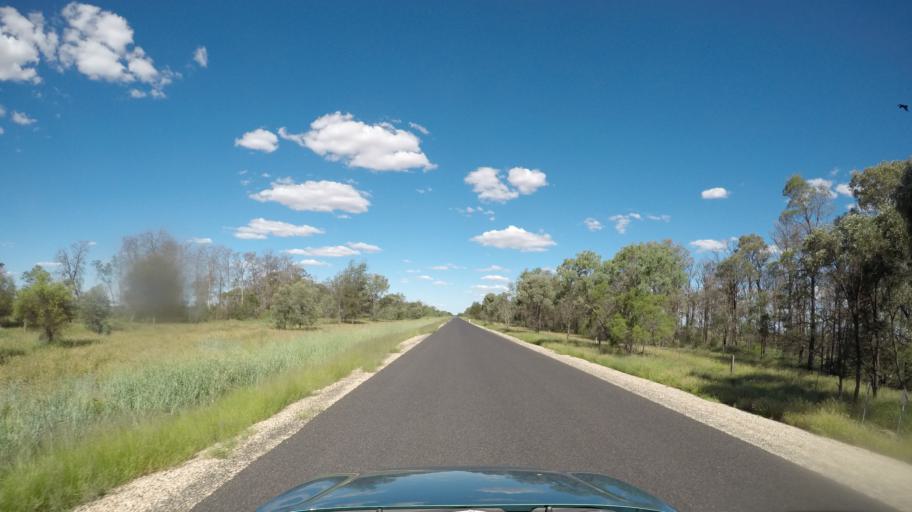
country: AU
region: Queensland
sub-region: Goondiwindi
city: Goondiwindi
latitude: -28.1674
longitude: 150.1895
